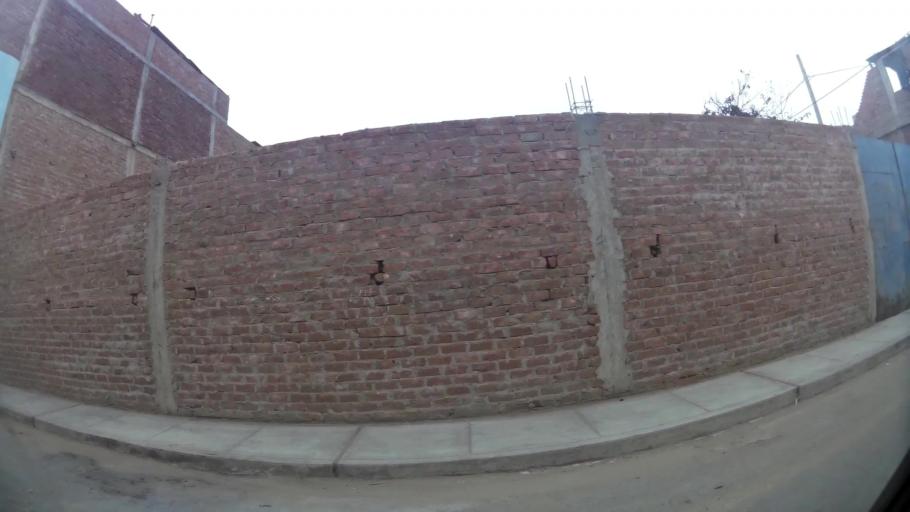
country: PE
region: La Libertad
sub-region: Provincia de Trujillo
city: Trujillo
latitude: -8.1042
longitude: -79.0436
